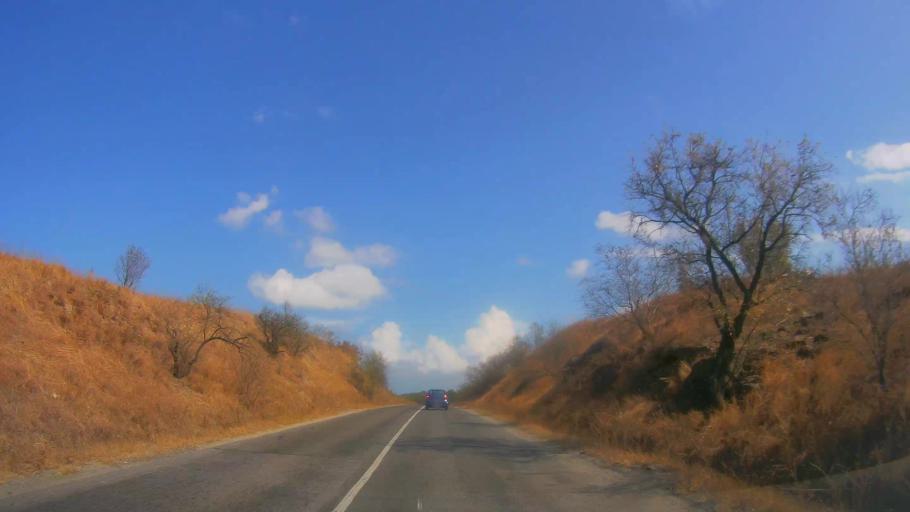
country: BG
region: Burgas
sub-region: Obshtina Burgas
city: Burgas
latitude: 42.4768
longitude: 27.3928
